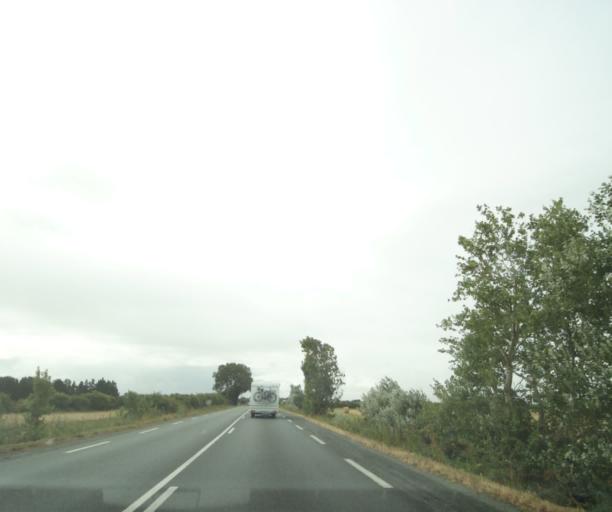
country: FR
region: Pays de la Loire
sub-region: Departement de la Vendee
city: Sainte-Gemme-la-Plaine
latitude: 46.4316
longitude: -1.0968
